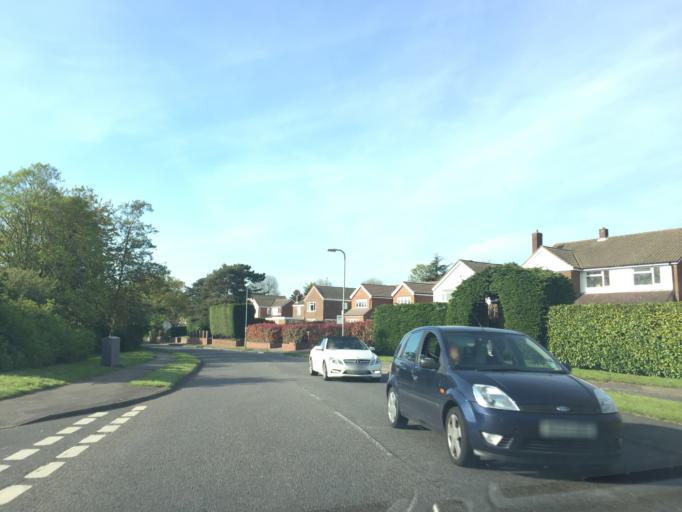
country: GB
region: England
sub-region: Essex
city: Harlow
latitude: 51.7530
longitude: 0.0813
